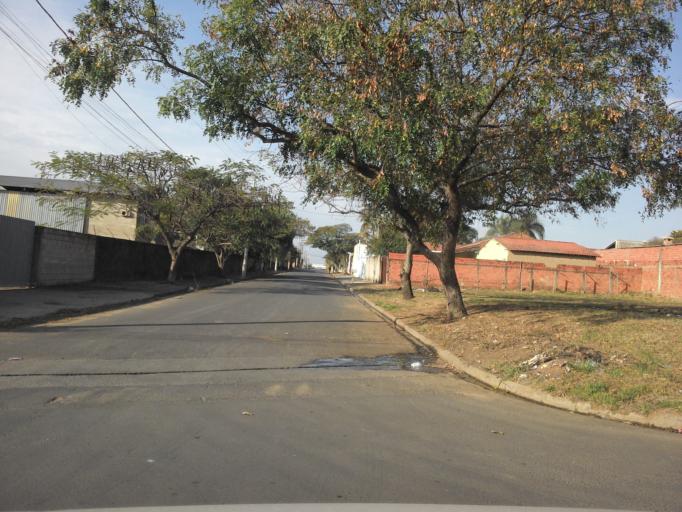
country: BR
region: Sao Paulo
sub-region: Hortolandia
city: Hortolandia
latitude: -22.9111
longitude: -47.2108
